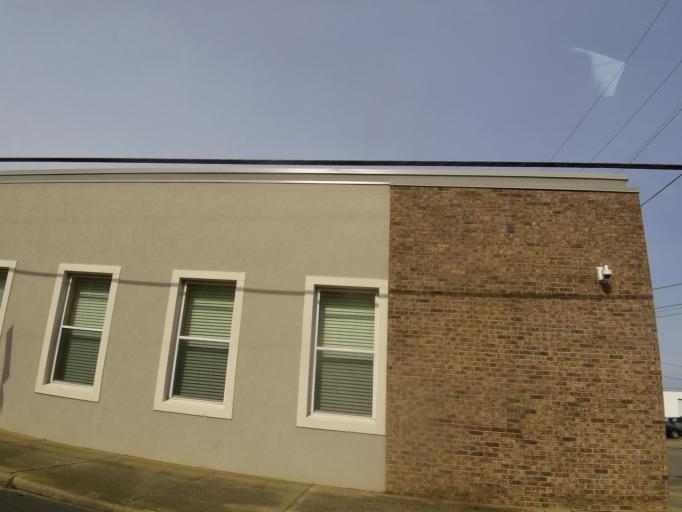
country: US
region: Alabama
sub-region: Houston County
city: Dothan
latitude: 31.2291
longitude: -85.3930
